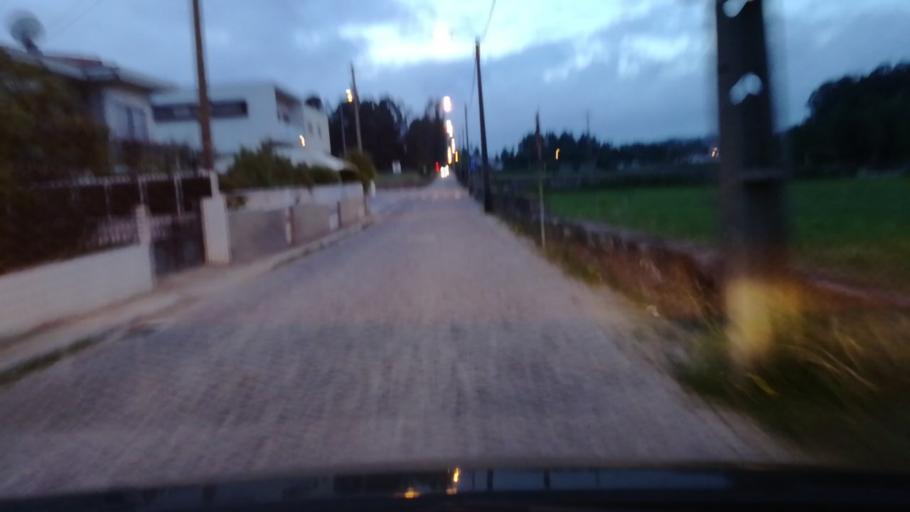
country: PT
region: Porto
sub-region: Maia
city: Anta
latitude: 41.2560
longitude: -8.6086
